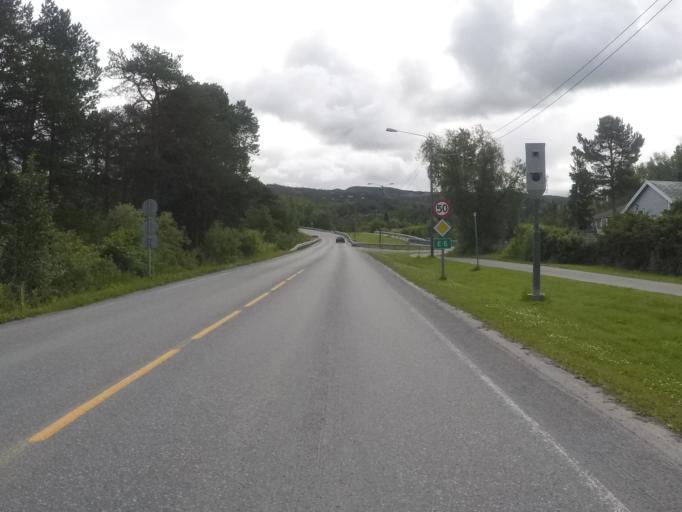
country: NO
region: Finnmark Fylke
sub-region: Alta
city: Alta
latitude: 69.9621
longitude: 23.3973
